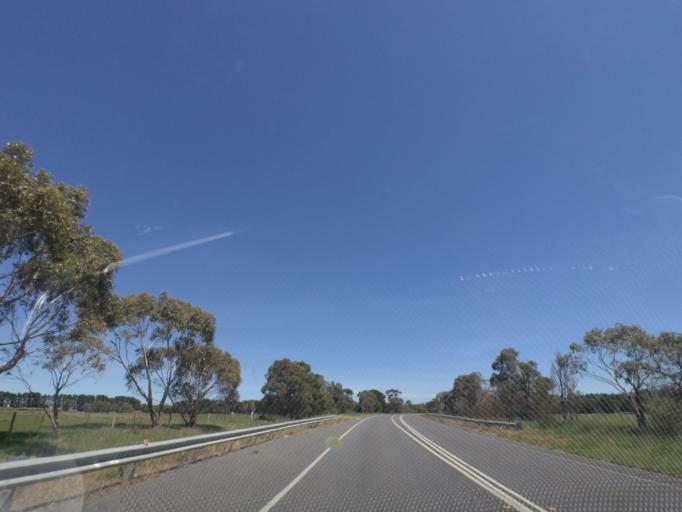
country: AU
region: Victoria
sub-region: Hume
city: Sunbury
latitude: -37.5426
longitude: 144.6332
